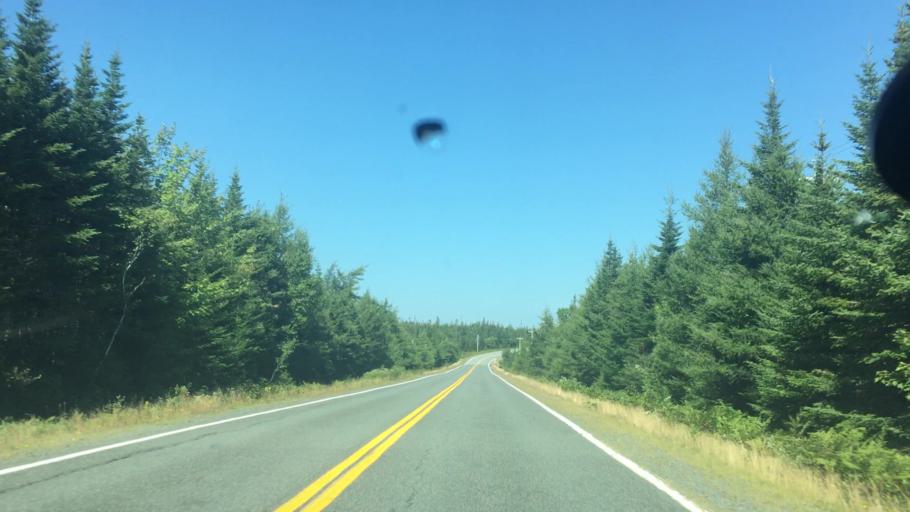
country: CA
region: Nova Scotia
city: Antigonish
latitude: 45.0054
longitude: -62.1037
